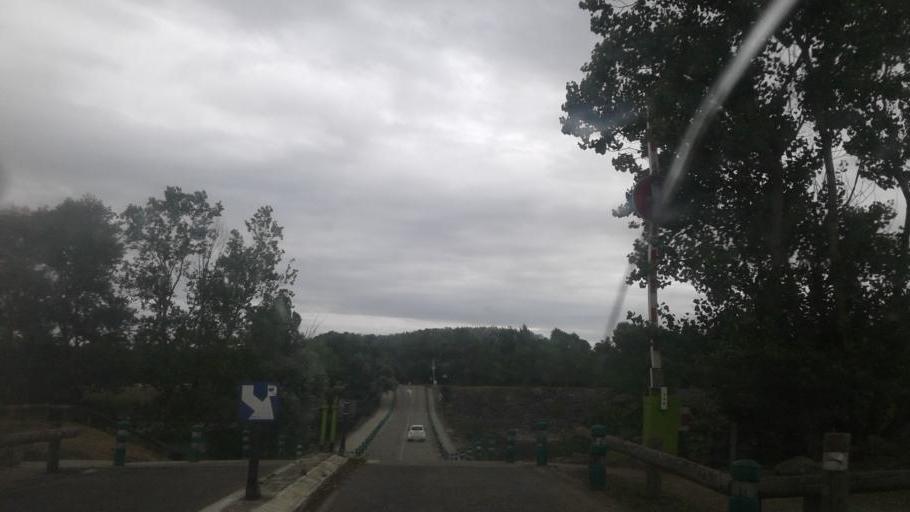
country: FR
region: Rhone-Alpes
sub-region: Departement du Rhone
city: Vaulx-en-Velin
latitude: 45.8050
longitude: 4.9333
